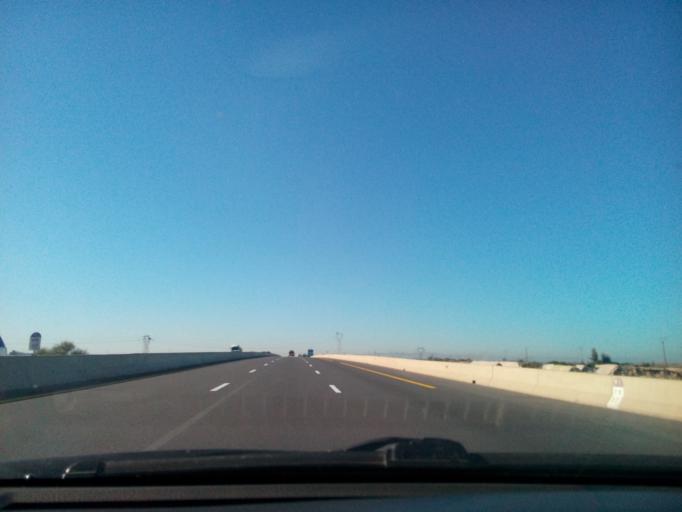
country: DZ
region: Relizane
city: Djidiouia
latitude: 35.9248
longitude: 0.7841
